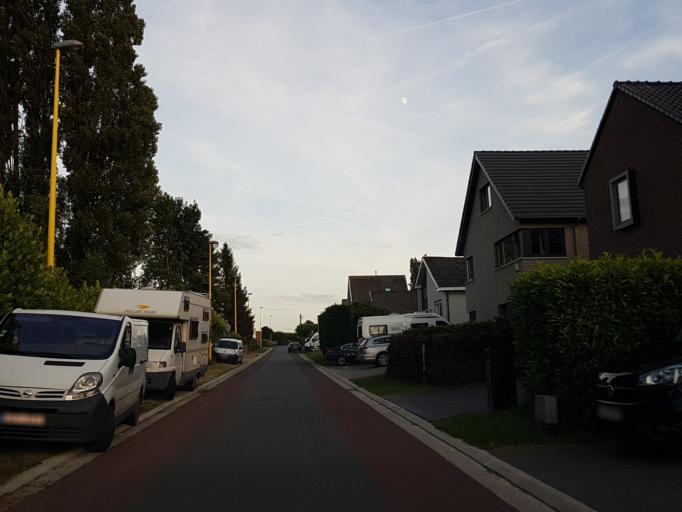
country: BE
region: Flanders
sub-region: Provincie Vlaams-Brabant
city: Meise
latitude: 50.9538
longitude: 4.2923
